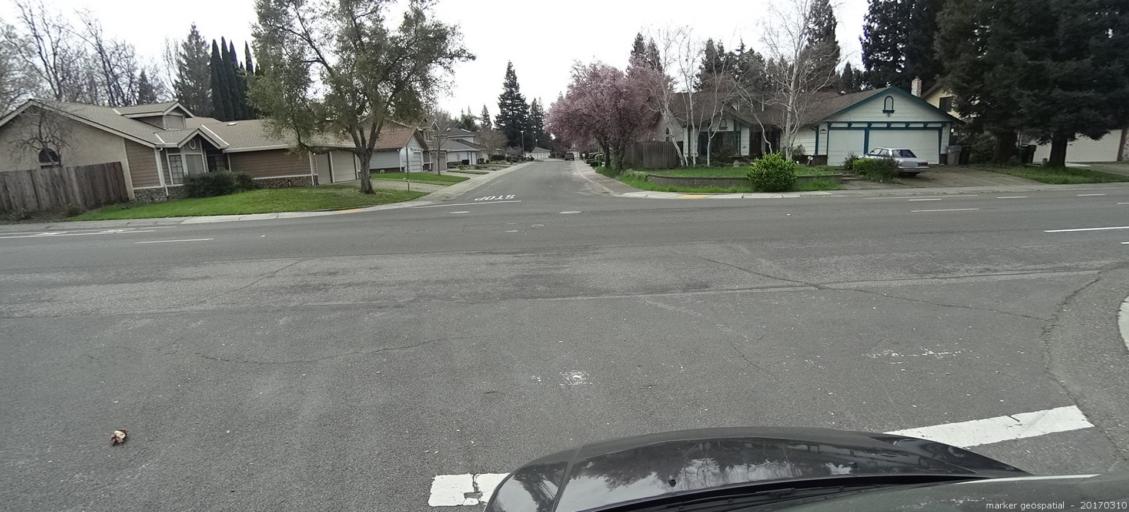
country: US
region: California
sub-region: Sacramento County
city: Parkway
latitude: 38.4881
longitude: -121.5204
